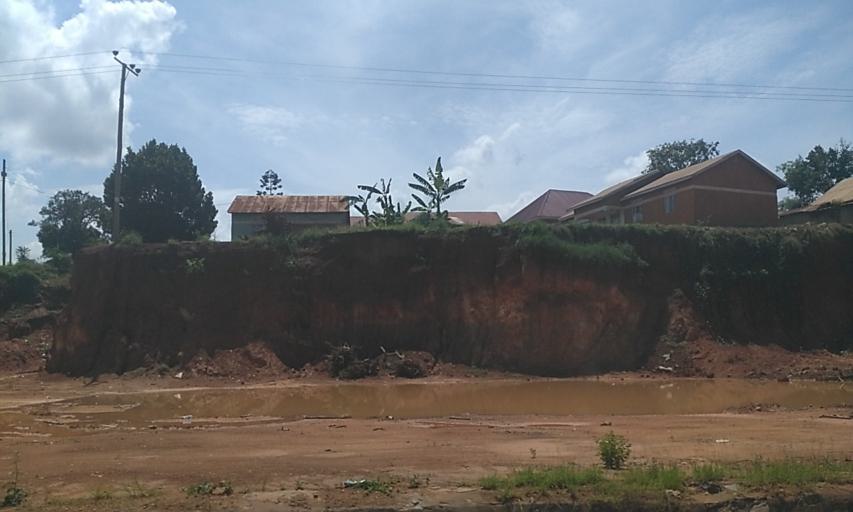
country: UG
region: Central Region
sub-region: Wakiso District
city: Wakiso
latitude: 0.3973
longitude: 32.4872
